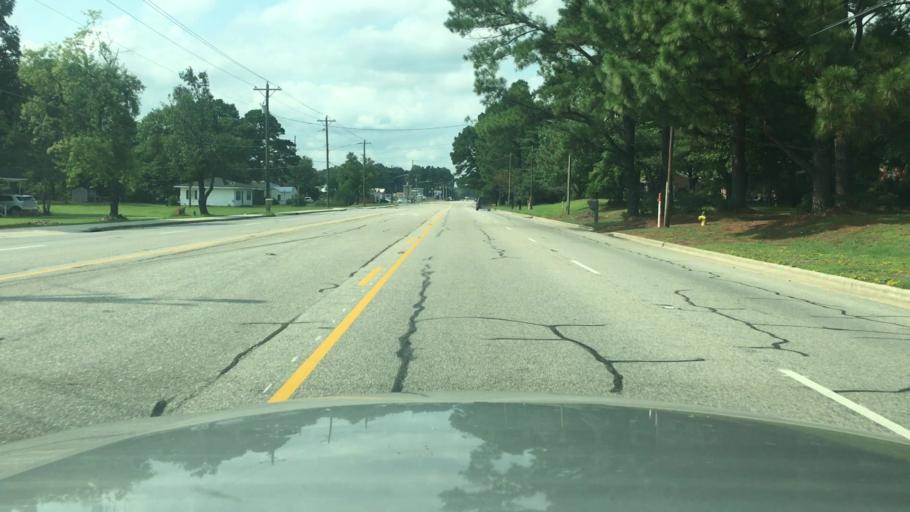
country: US
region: North Carolina
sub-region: Cumberland County
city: Fayetteville
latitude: 35.0249
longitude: -78.8422
